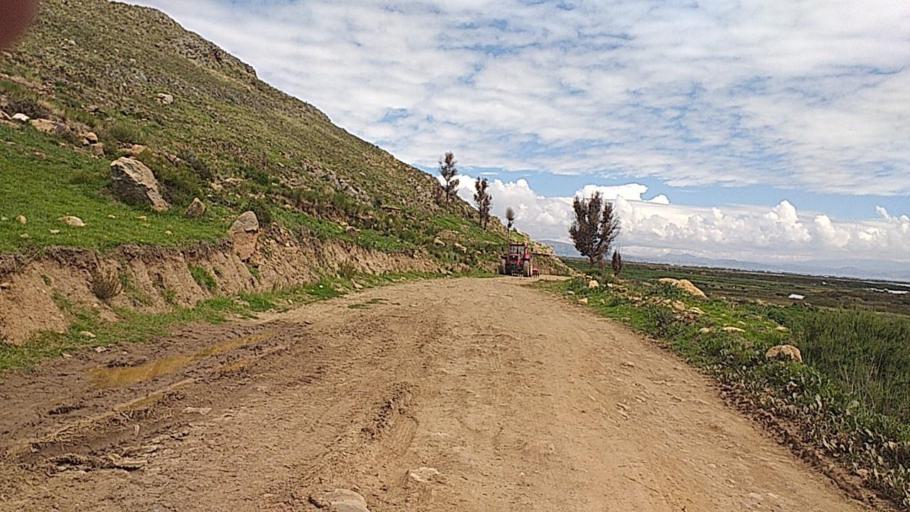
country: BO
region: La Paz
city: Batallas
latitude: -16.3402
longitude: -68.6358
